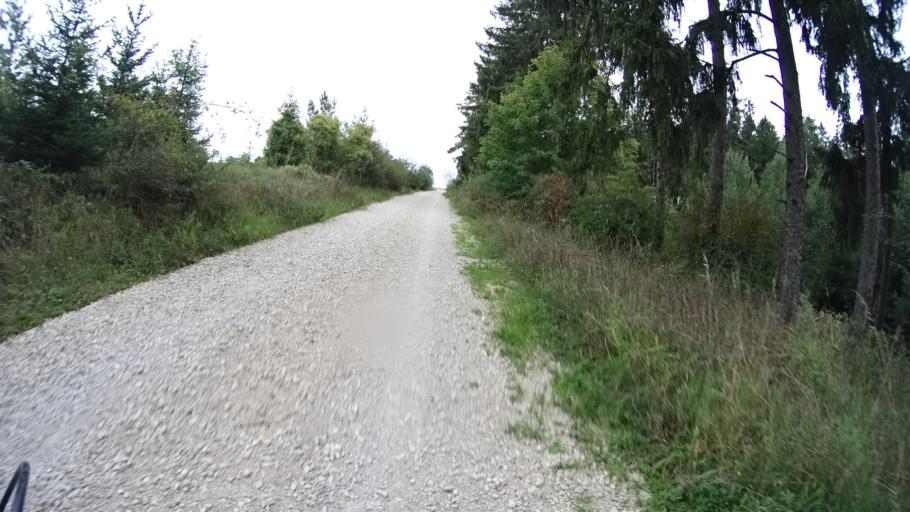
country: DE
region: Bavaria
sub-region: Upper Bavaria
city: Bohmfeld
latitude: 48.8512
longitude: 11.3476
